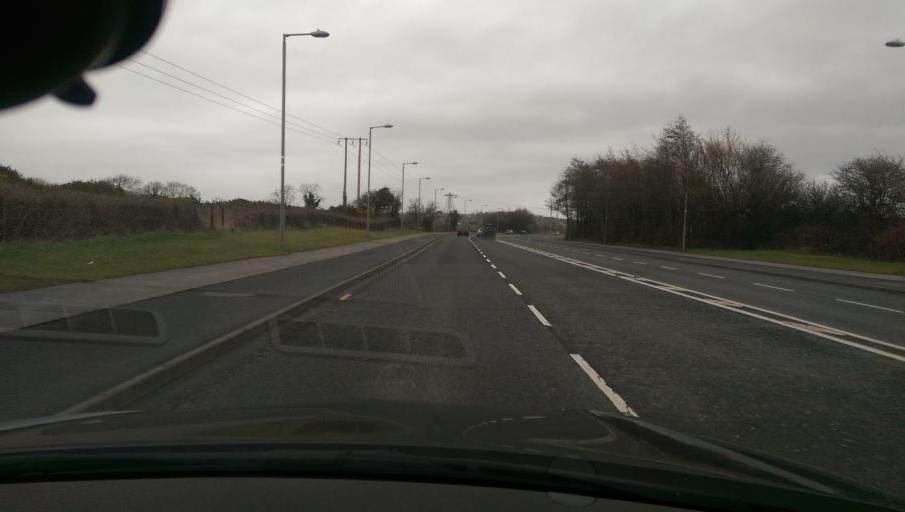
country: IE
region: Connaught
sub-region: County Galway
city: Gaillimh
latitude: 53.2895
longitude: -9.0355
